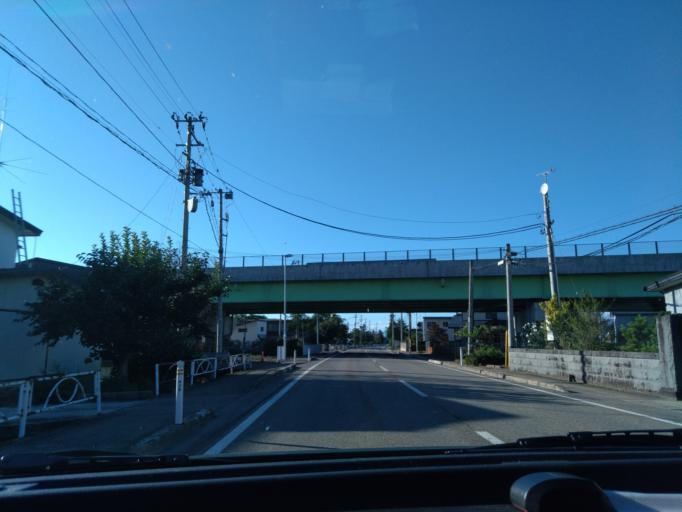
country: JP
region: Akita
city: Omagari
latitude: 39.4364
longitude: 140.4823
